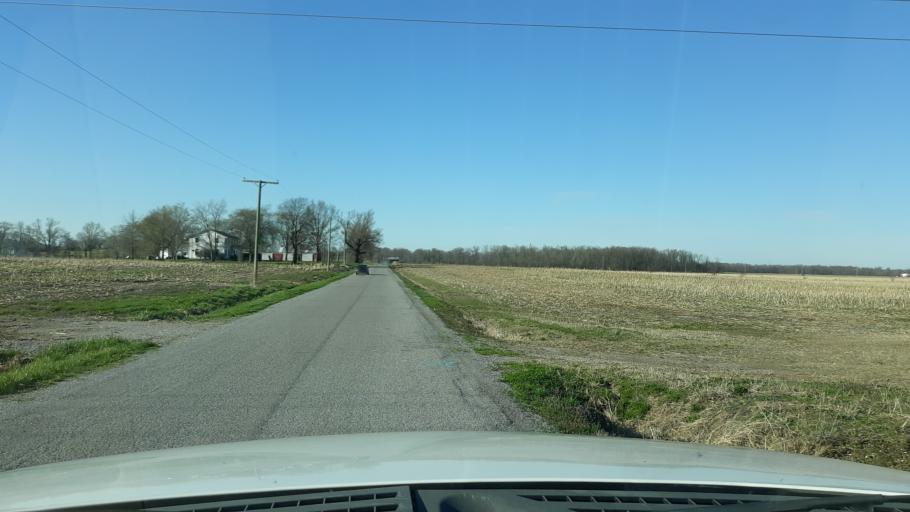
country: US
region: Illinois
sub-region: Saline County
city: Harrisburg
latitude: 37.7681
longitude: -88.5864
